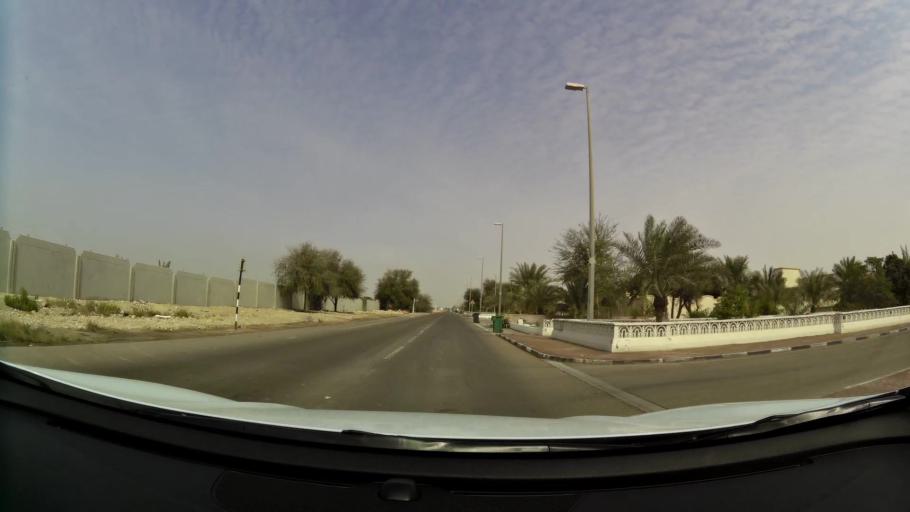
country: AE
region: Abu Dhabi
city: Abu Dhabi
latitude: 24.5305
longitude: 54.6663
